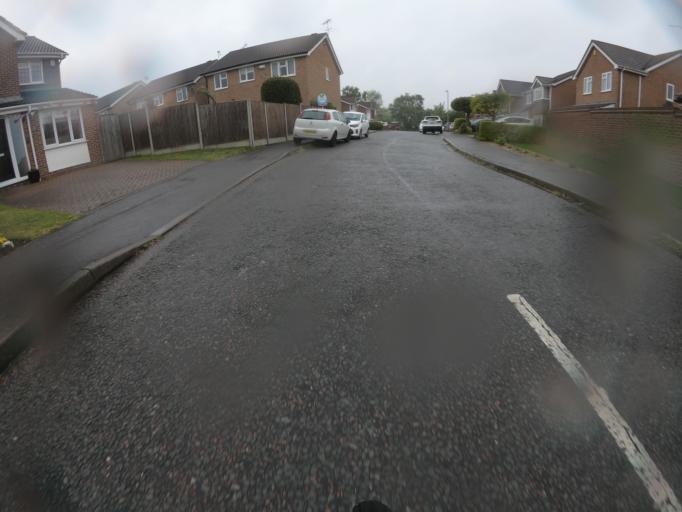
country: GB
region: England
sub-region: Kent
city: Gravesend
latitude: 51.4293
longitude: 0.3472
